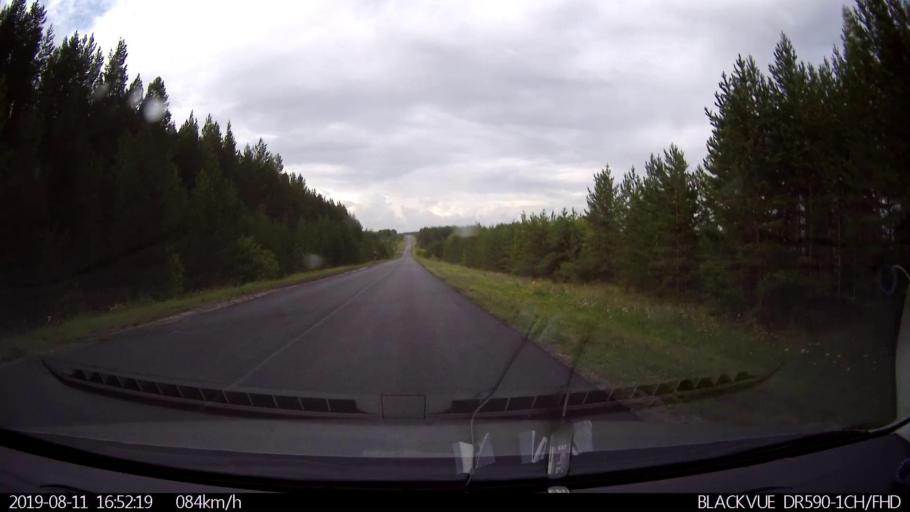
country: RU
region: Ulyanovsk
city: Mayna
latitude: 54.2466
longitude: 47.6746
